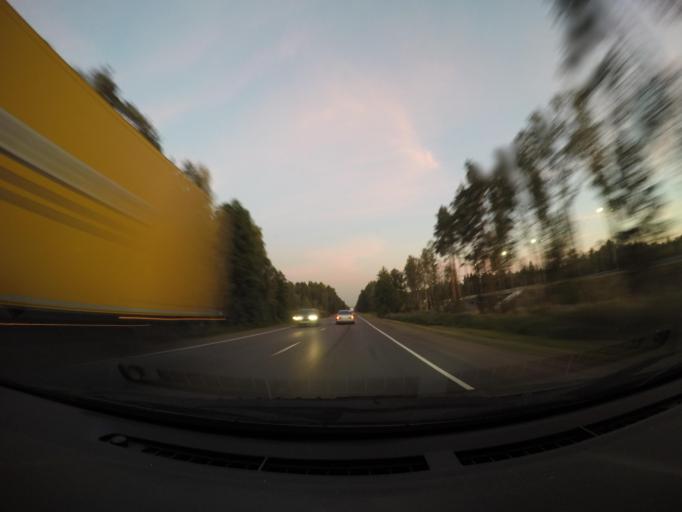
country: RU
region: Moskovskaya
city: Gzhel'
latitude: 55.5606
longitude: 38.3964
